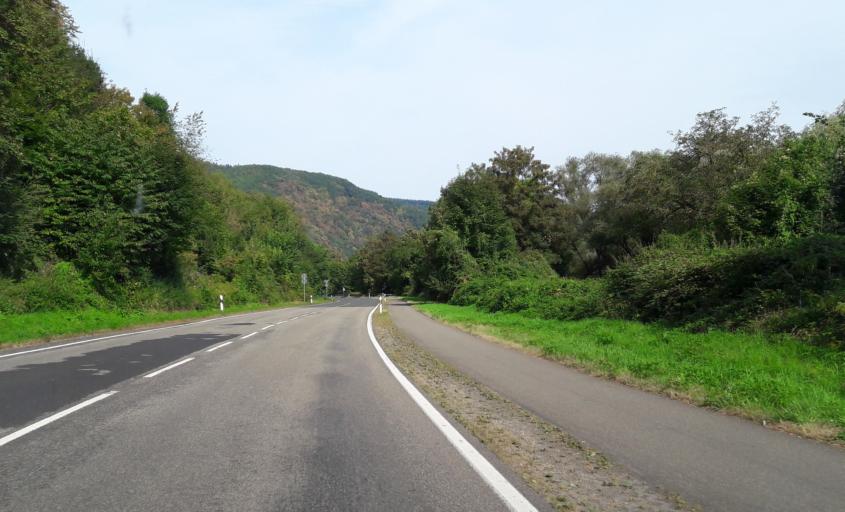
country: DE
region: Rheinland-Pfalz
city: Nehren
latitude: 50.0905
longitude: 7.1975
